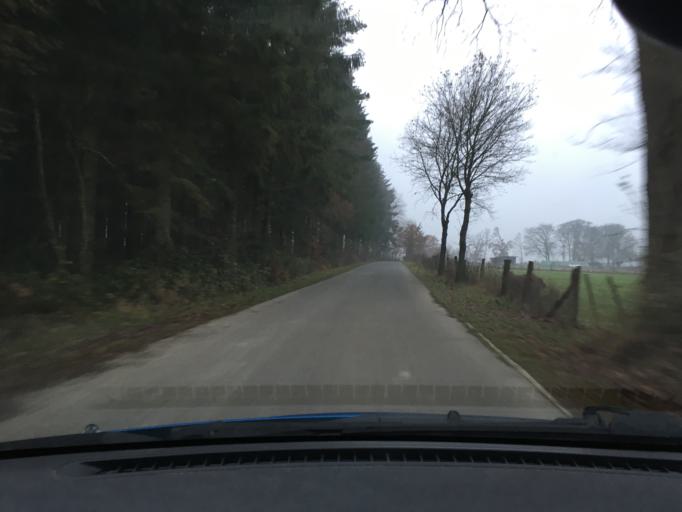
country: DE
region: Lower Saxony
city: Soderstorf
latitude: 53.1532
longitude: 10.1702
